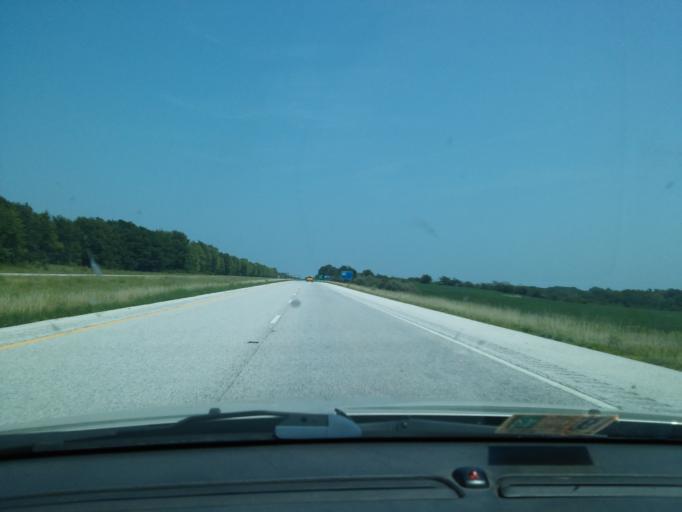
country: US
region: Illinois
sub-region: Morgan County
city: South Jacksonville
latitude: 39.6814
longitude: -90.2618
